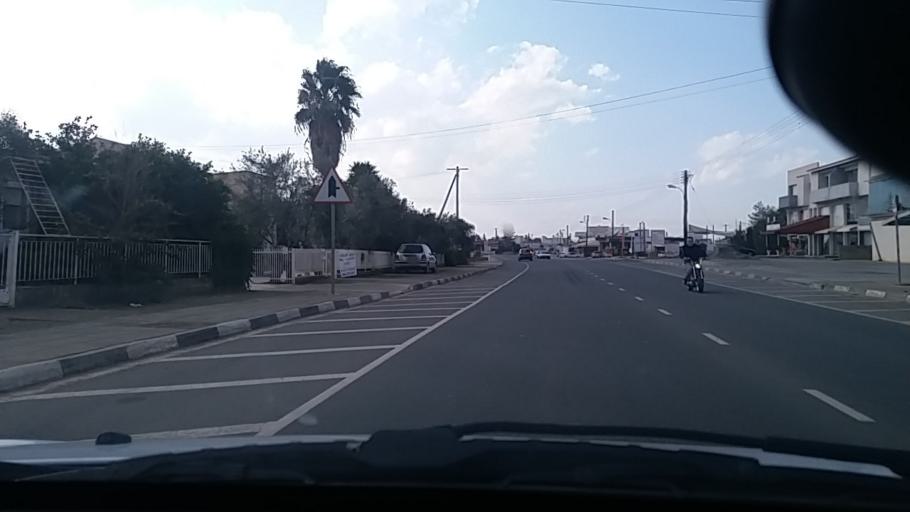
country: CY
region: Lefkosia
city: Kokkinotrimithia
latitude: 35.1486
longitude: 33.2099
